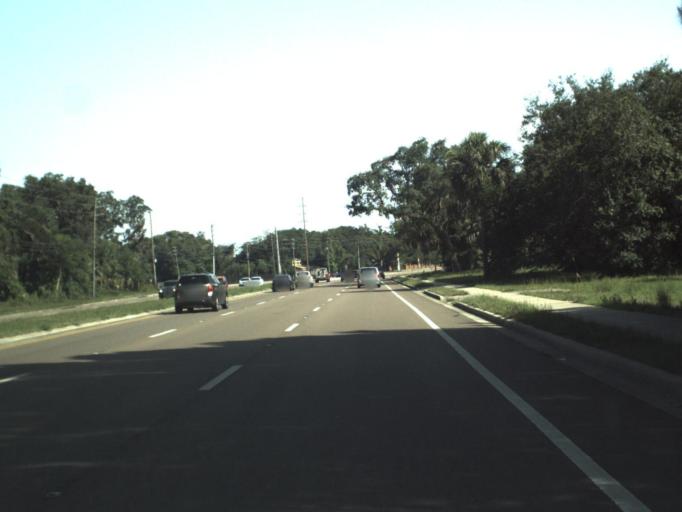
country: US
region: Florida
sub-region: Seminole County
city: Oviedo
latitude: 28.6360
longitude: -81.2079
